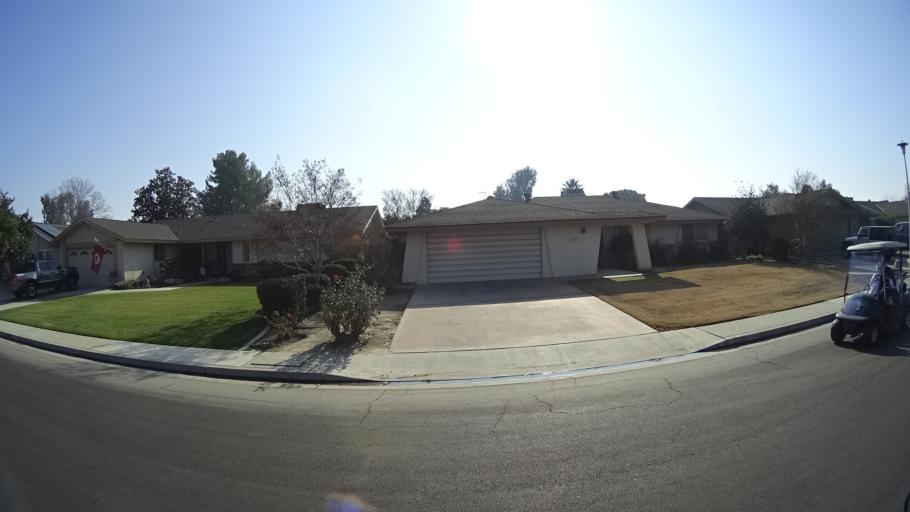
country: US
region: California
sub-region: Kern County
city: Greenacres
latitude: 35.3533
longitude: -119.0697
